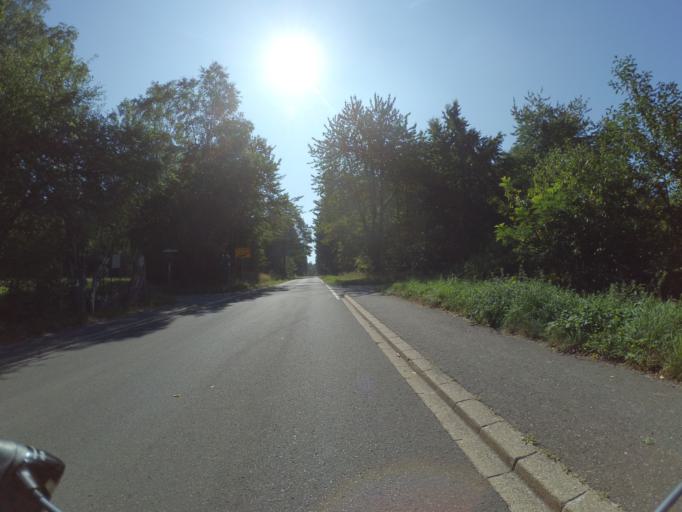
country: DE
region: Rheinland-Pfalz
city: Morbach
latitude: 49.7730
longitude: 7.1038
